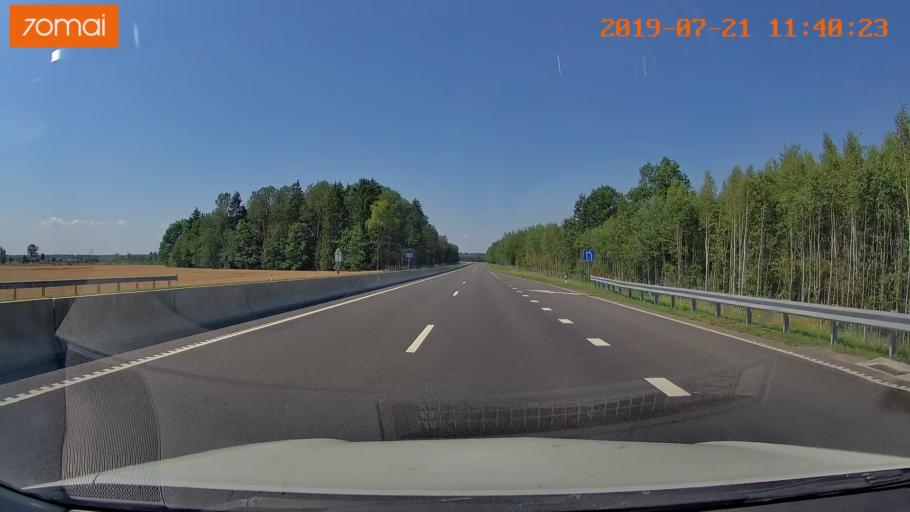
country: BY
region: Grodnenskaya
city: Lyubcha
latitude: 53.9547
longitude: 26.1760
